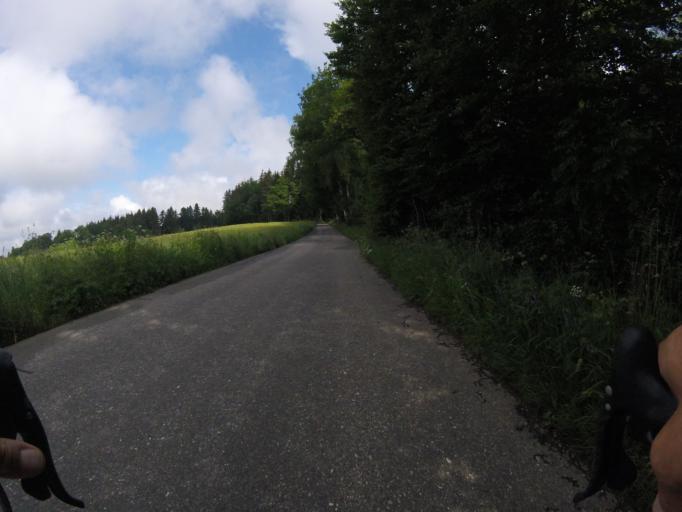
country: CH
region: Bern
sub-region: Bern-Mittelland District
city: Walkringen
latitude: 46.9604
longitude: 7.5984
